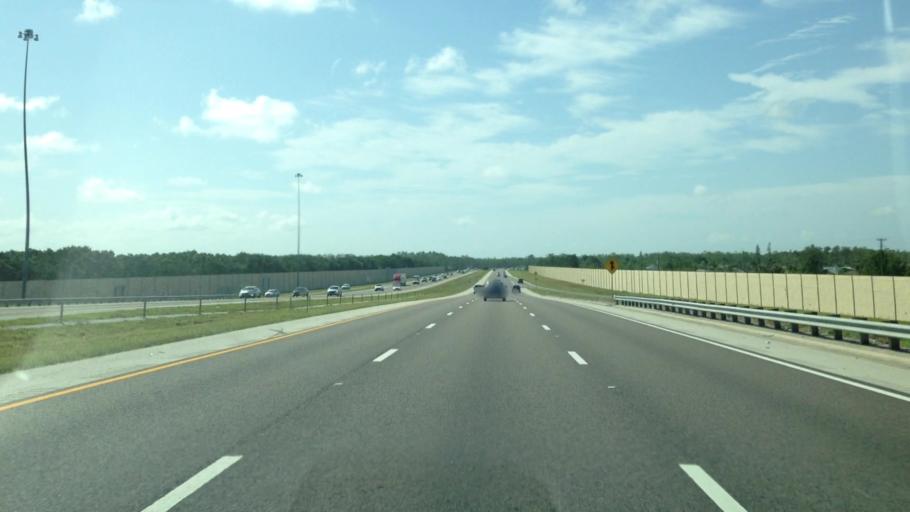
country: US
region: Florida
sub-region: Lee County
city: Estero
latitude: 26.4312
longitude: -81.7776
